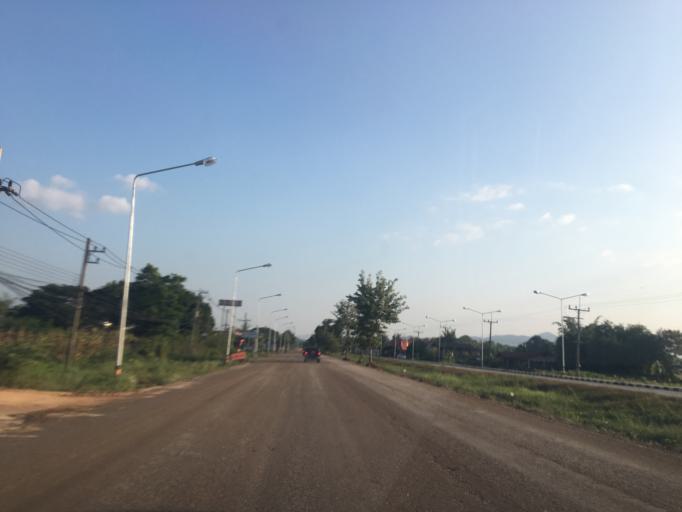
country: TH
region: Lampang
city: Ngao
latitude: 18.7505
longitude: 99.9715
